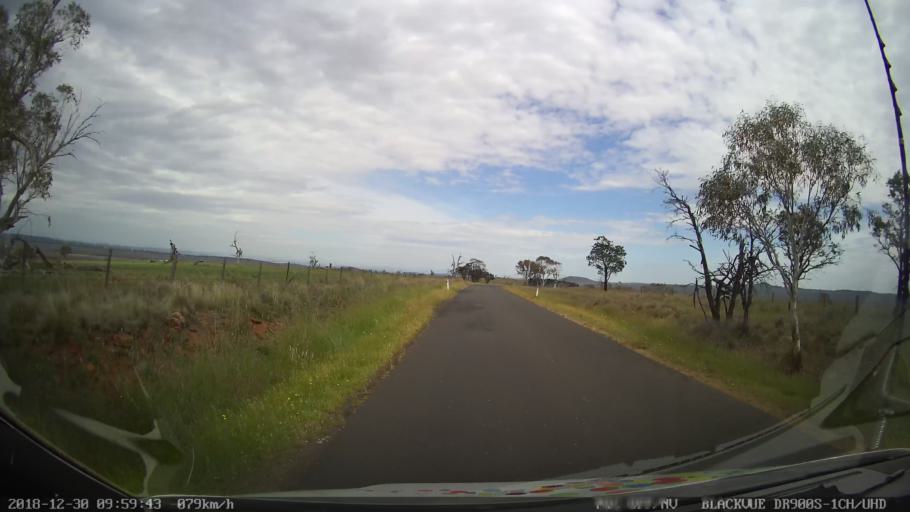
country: AU
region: New South Wales
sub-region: Cooma-Monaro
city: Cooma
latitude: -36.5217
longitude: 149.2062
